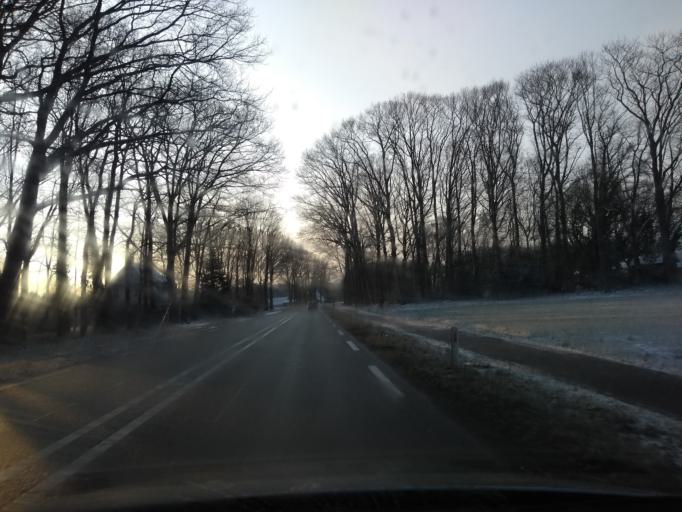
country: NL
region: Overijssel
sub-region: Gemeente Hof van Twente
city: Delden
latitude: 52.2874
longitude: 6.6698
